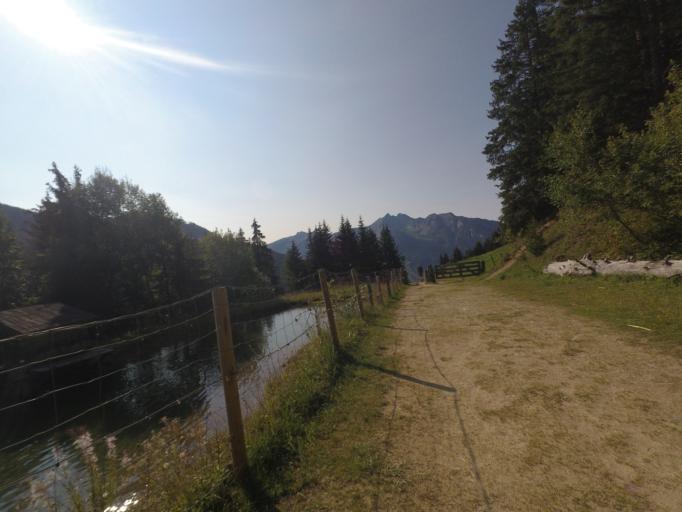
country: AT
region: Salzburg
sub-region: Politischer Bezirk Sankt Johann im Pongau
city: Kleinarl
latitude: 47.2715
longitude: 13.2588
